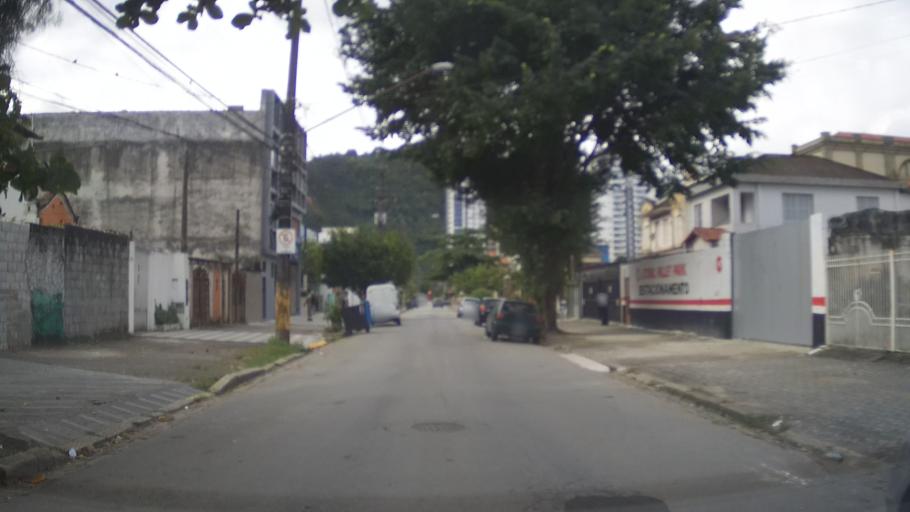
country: BR
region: Sao Paulo
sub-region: Santos
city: Santos
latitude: -23.9476
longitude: -46.3317
